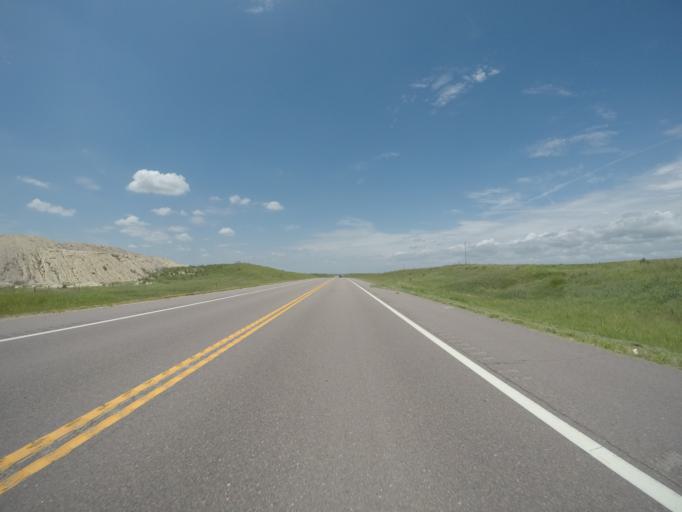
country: US
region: Kansas
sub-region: Graham County
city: Hill City
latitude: 39.3792
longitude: -99.7389
